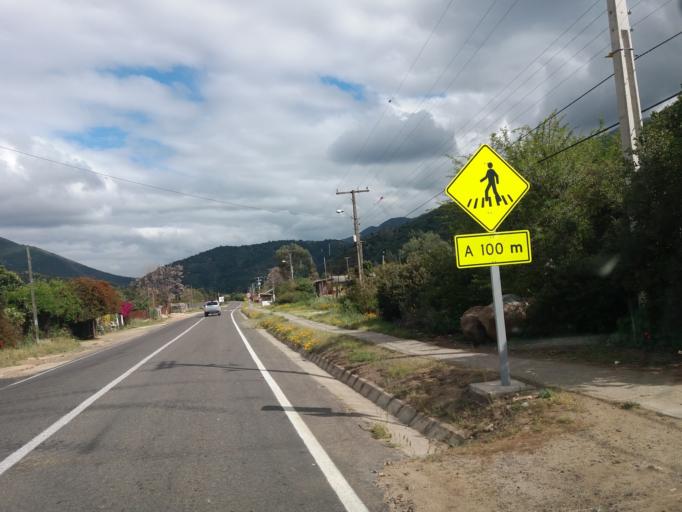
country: CL
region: Valparaiso
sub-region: Provincia de Marga Marga
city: Limache
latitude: -33.0567
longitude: -71.0865
